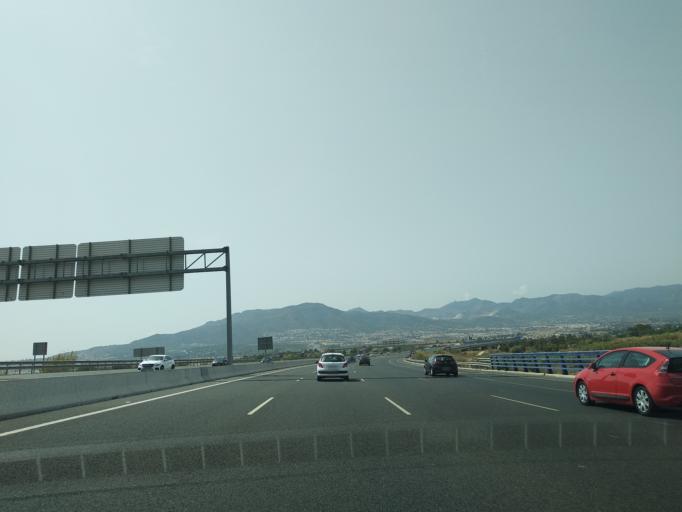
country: ES
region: Andalusia
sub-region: Provincia de Malaga
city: Alhaurin de la Torre
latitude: 36.7021
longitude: -4.5153
